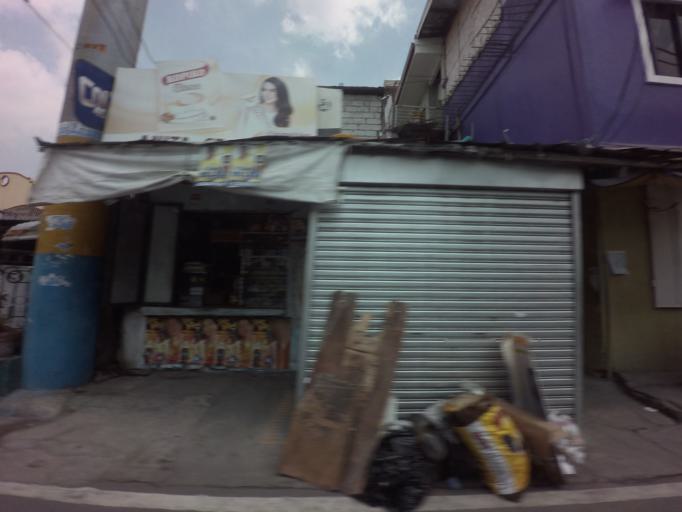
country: PH
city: Sambayanihan People's Village
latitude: 14.4582
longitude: 121.0534
